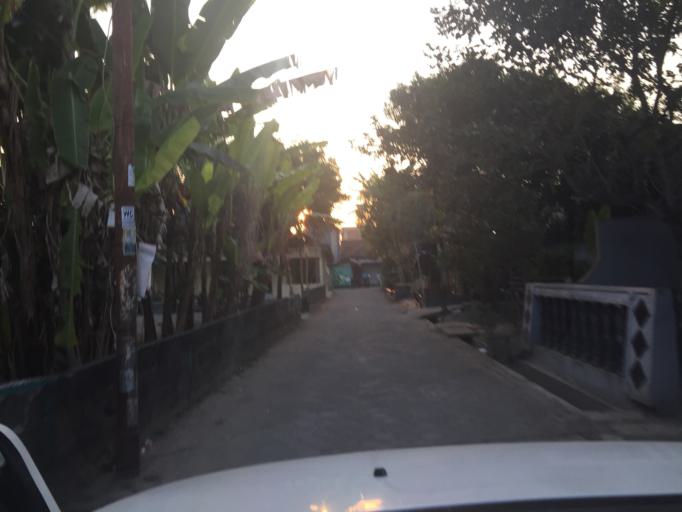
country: ID
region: Daerah Istimewa Yogyakarta
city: Gamping Lor
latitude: -7.7913
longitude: 110.3295
